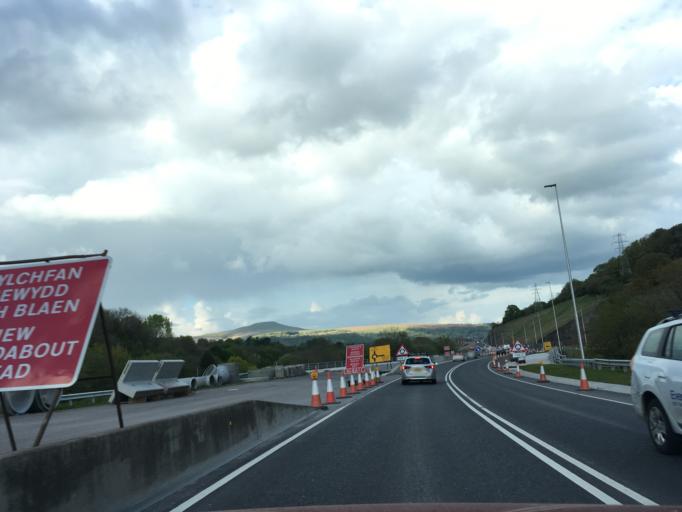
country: GB
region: Wales
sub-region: Monmouthshire
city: Gilwern
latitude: 51.8156
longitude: -3.1171
